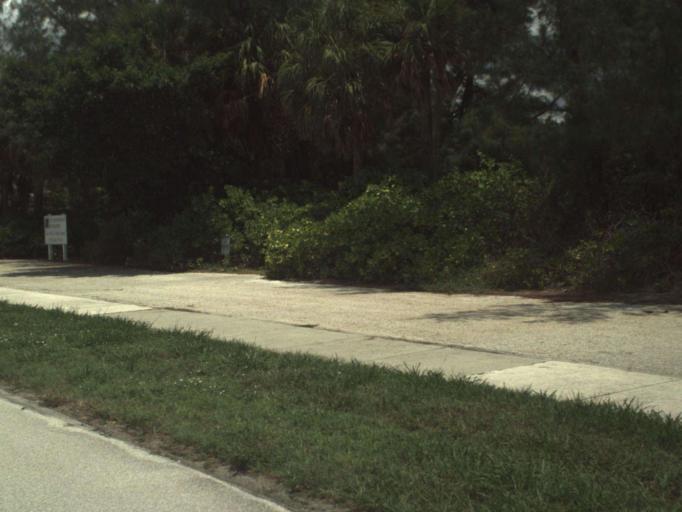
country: US
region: Florida
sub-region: Martin County
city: Sewall's Point
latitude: 27.2270
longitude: -80.1823
